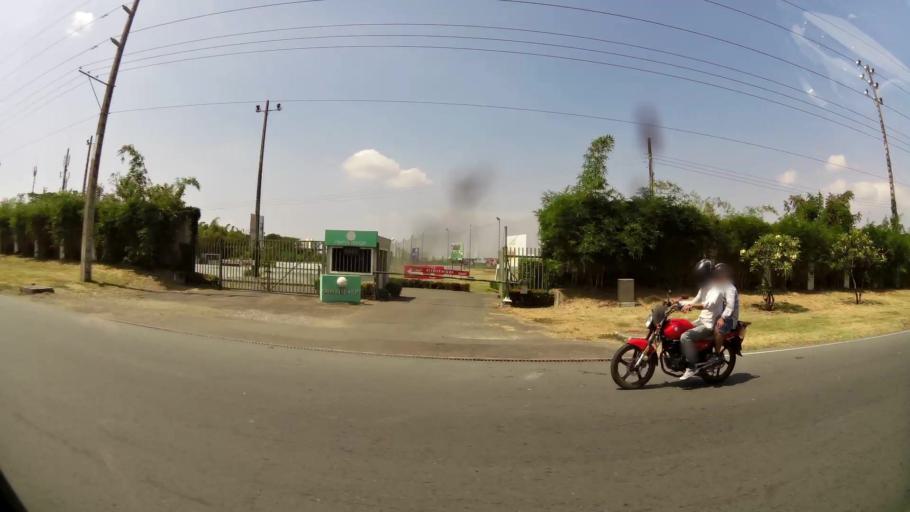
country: EC
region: Guayas
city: Eloy Alfaro
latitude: -2.0984
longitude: -79.8738
